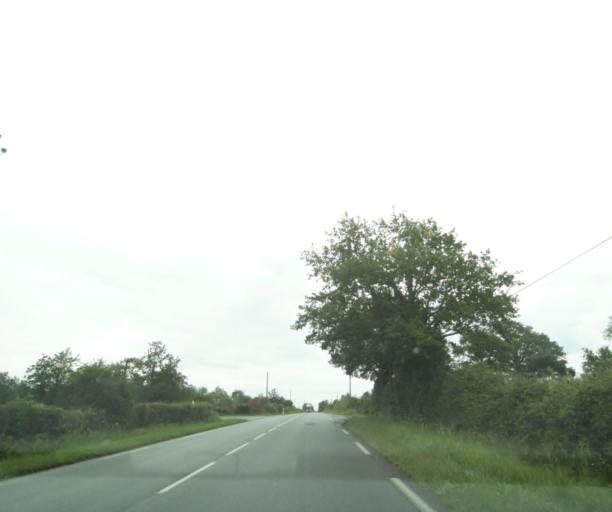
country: FR
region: Poitou-Charentes
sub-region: Departement des Deux-Sevres
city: Viennay
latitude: 46.6974
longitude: -0.2414
